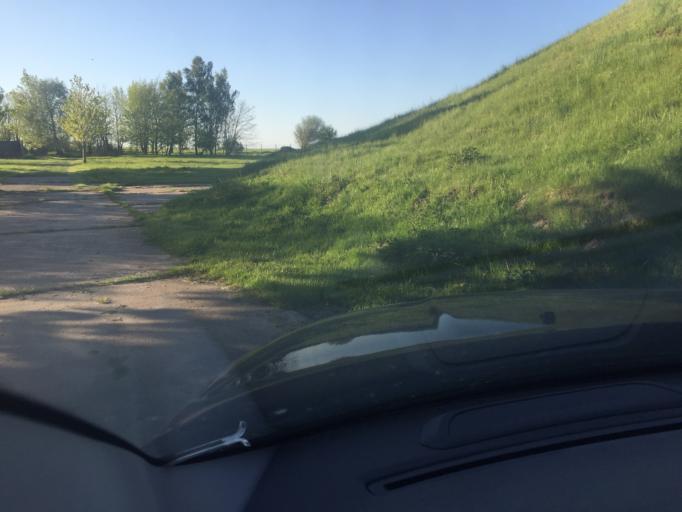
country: DE
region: Mecklenburg-Vorpommern
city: Saal
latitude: 54.3194
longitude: 12.4852
